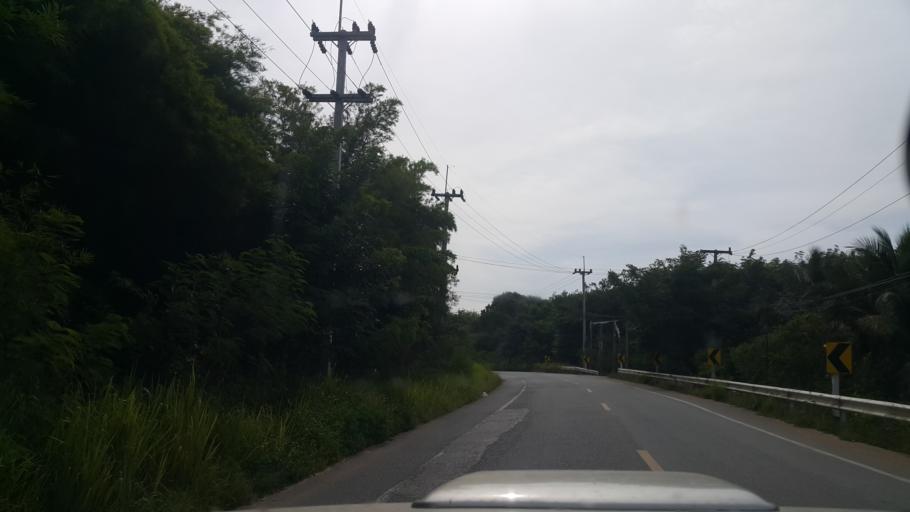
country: TH
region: Rayong
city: Ban Chang
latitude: 12.7686
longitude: 101.0073
